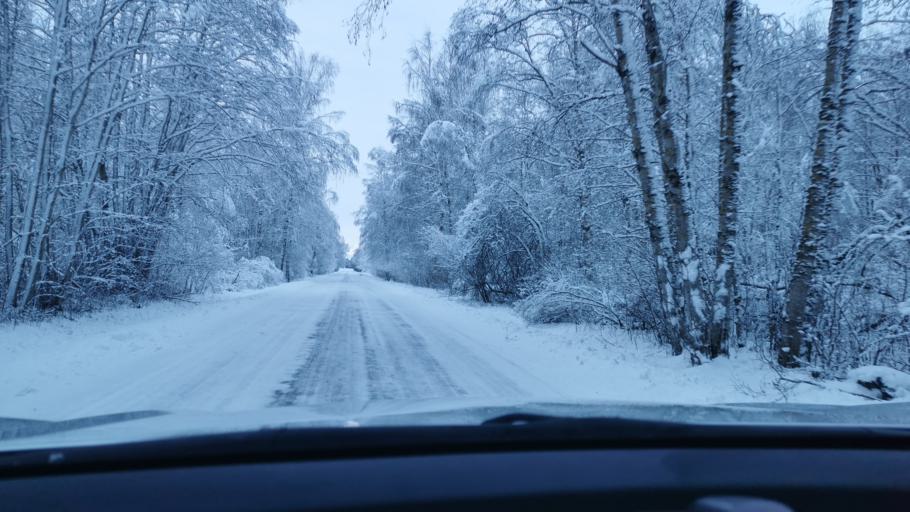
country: EE
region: Laeaene-Virumaa
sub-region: Viru-Nigula vald
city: Kunda
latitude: 59.4444
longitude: 26.5060
